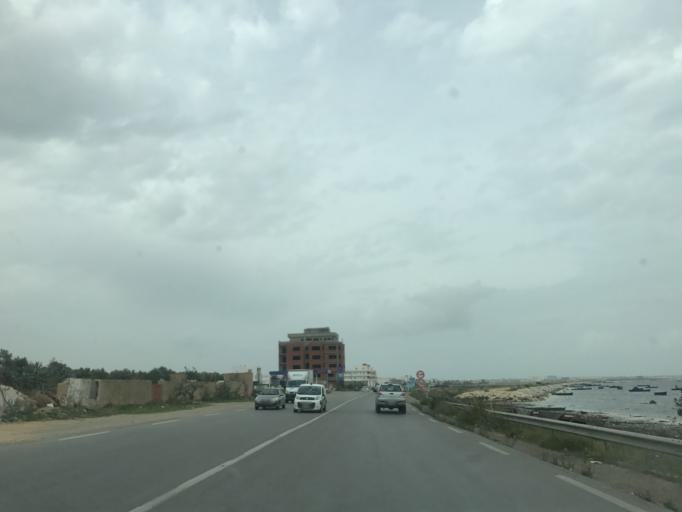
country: TN
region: Al Munastir
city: Qusaybat al Madyuni
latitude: 35.7005
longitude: 10.8290
